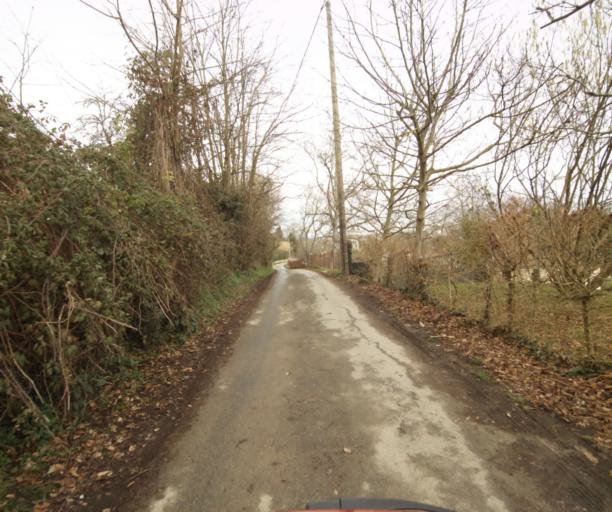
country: FR
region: Midi-Pyrenees
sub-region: Departement de l'Ariege
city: Pamiers
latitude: 43.1109
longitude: 1.6017
